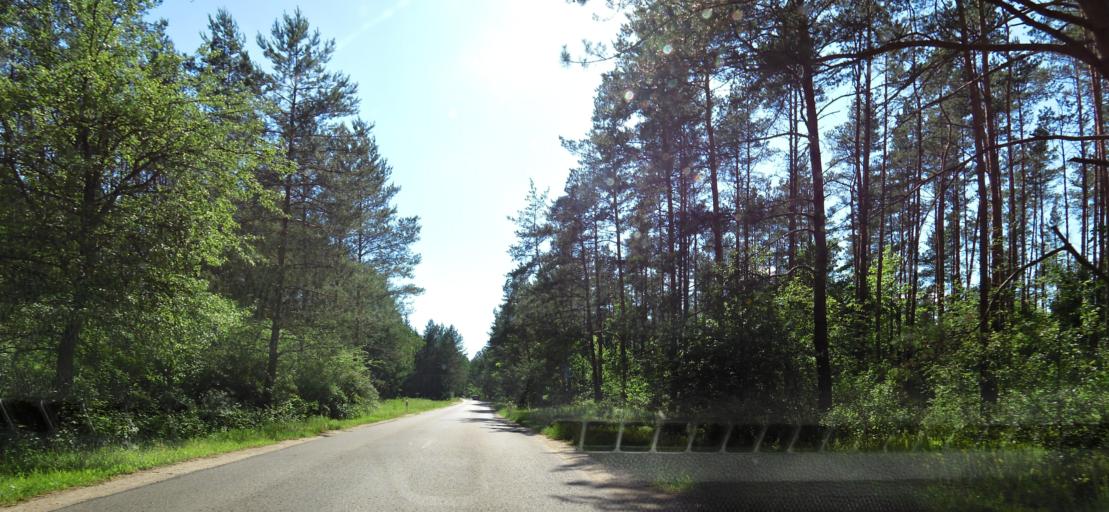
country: LT
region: Vilnius County
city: Rasos
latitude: 54.7538
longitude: 25.3335
